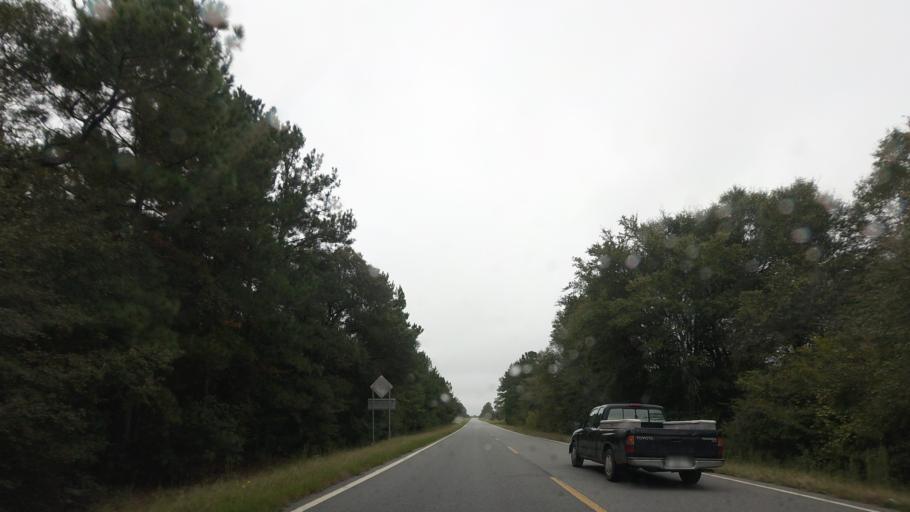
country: US
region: Georgia
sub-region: Berrien County
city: Enigma
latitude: 31.4370
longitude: -83.2414
